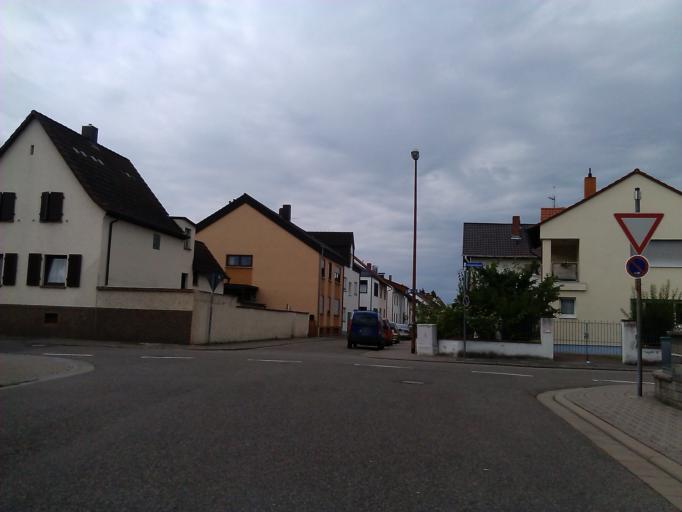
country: DE
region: Rheinland-Pfalz
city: Schifferstadt
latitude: 49.3773
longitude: 8.3847
